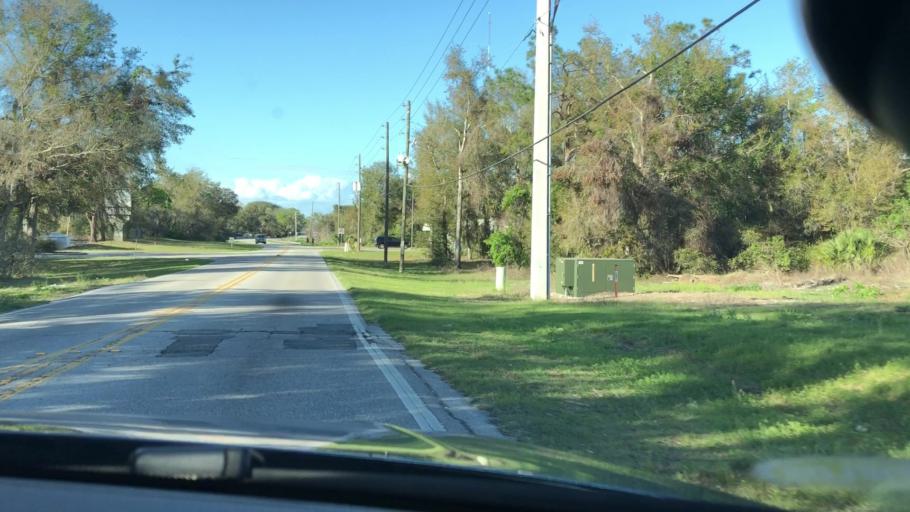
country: US
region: Florida
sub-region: Lake County
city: Silver Lake
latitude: 28.8277
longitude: -81.7870
